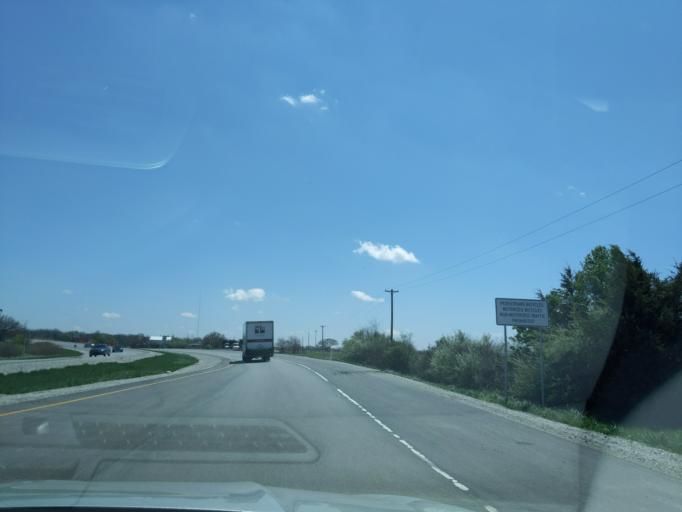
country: US
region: Indiana
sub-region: Boone County
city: Lebanon
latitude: 40.0739
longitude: -86.5024
